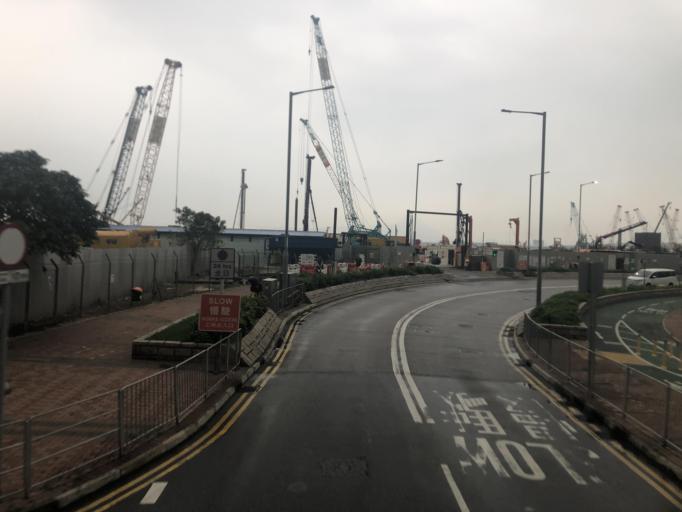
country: HK
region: Tuen Mun
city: Tuen Mun
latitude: 22.2965
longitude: 113.9518
